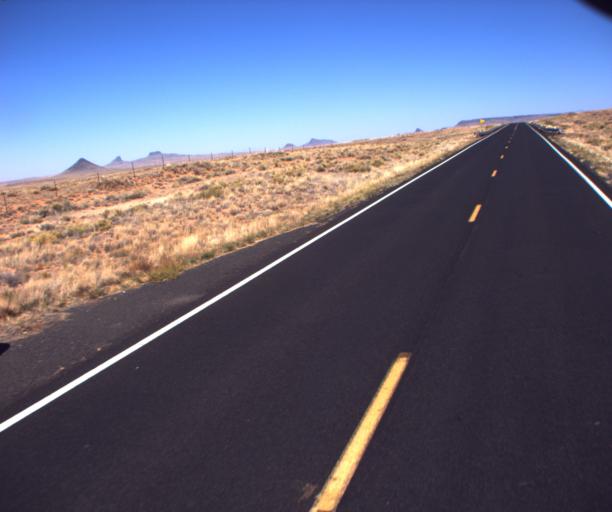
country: US
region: Arizona
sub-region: Navajo County
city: Dilkon
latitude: 35.2921
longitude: -110.4261
